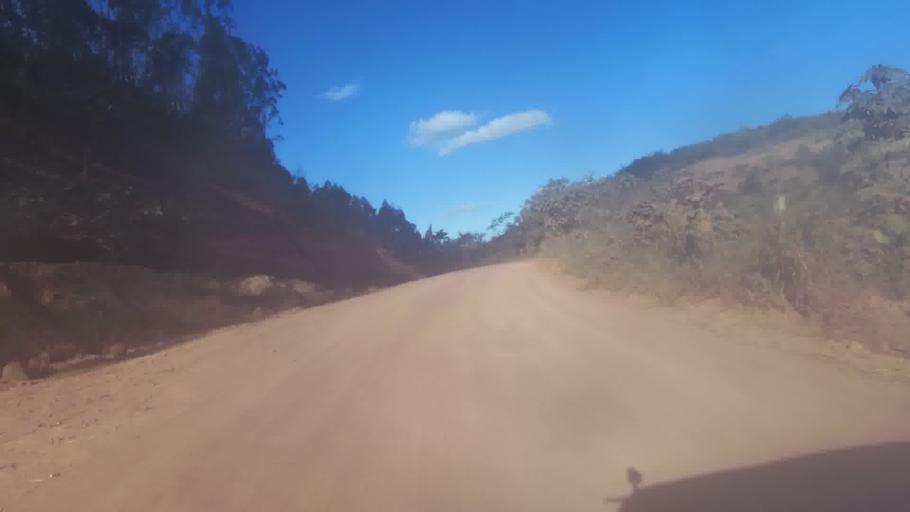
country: BR
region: Espirito Santo
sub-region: Mimoso Do Sul
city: Mimoso do Sul
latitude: -21.1023
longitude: -41.1368
